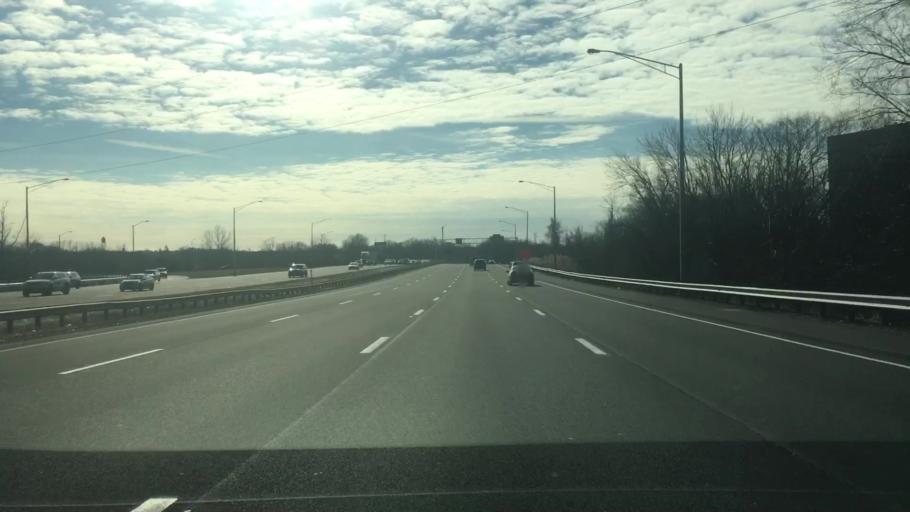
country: US
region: Connecticut
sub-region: Hartford County
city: Wethersfield
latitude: 41.6827
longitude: -72.6503
